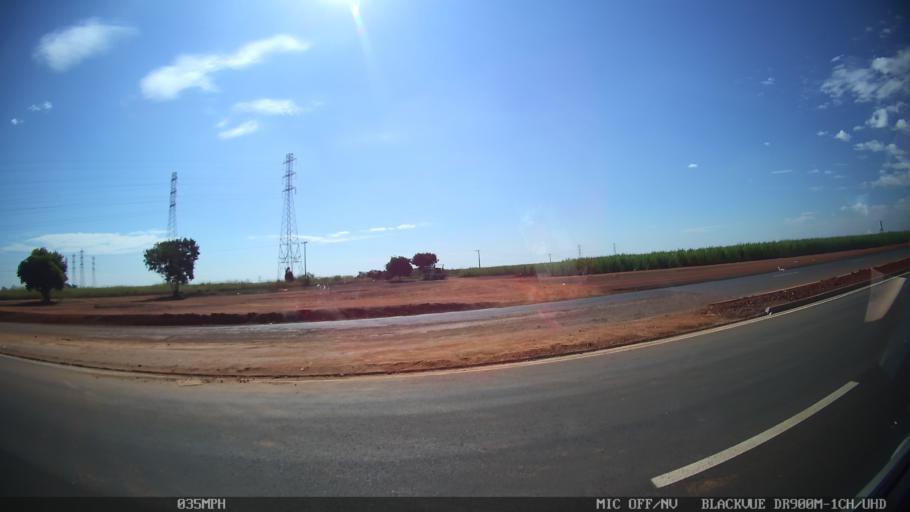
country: BR
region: Sao Paulo
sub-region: Santa Barbara D'Oeste
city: Santa Barbara d'Oeste
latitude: -22.7246
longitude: -47.4110
